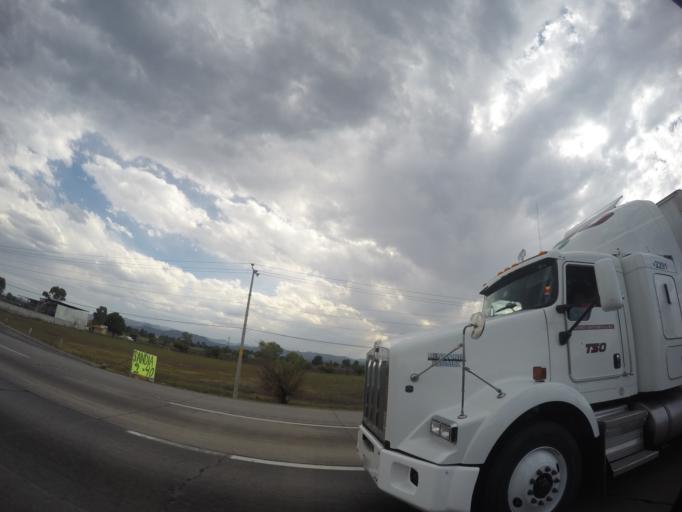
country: MX
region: Queretaro
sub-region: San Juan del Rio
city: Vista Hermosa (Cuasinada)
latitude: 20.3896
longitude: -100.0196
